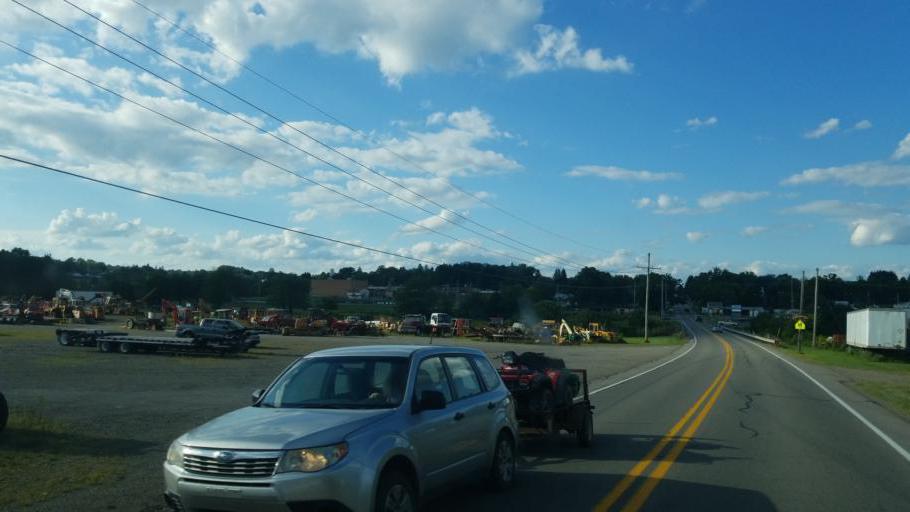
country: US
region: Pennsylvania
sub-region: Clarion County
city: Knox
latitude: 41.2275
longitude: -79.5287
